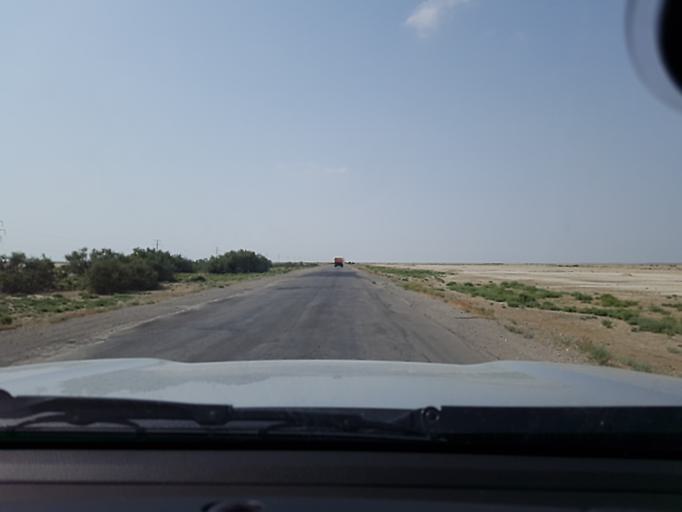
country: TM
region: Balkan
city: Gumdag
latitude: 38.9215
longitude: 54.5911
